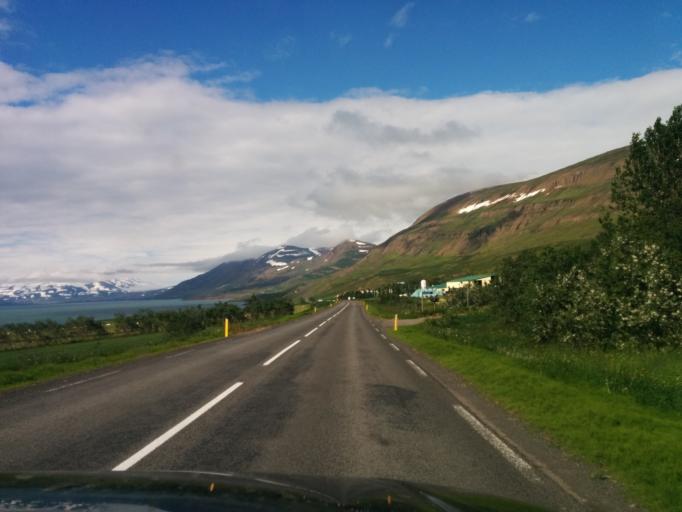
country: IS
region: Northeast
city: Akureyri
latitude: 65.7762
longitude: -18.0690
